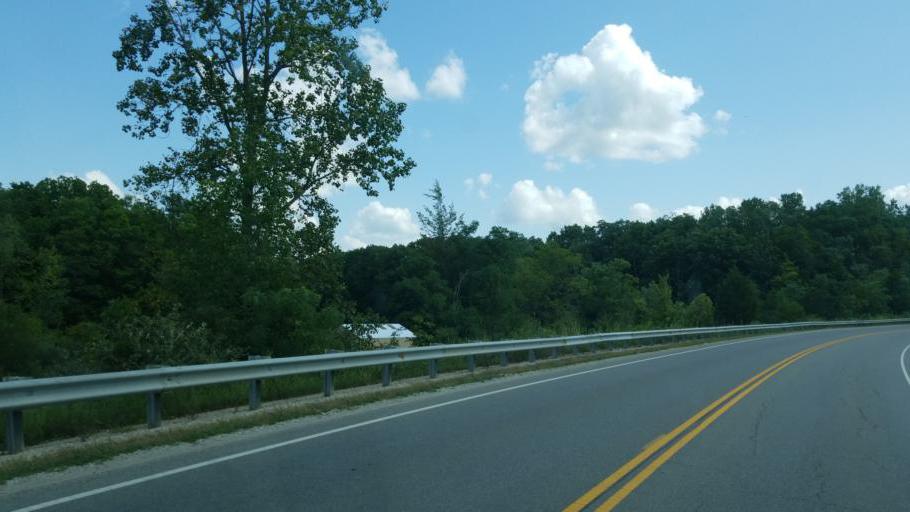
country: US
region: Ohio
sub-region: Delaware County
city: Lewis Center
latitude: 40.2298
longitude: -82.9819
